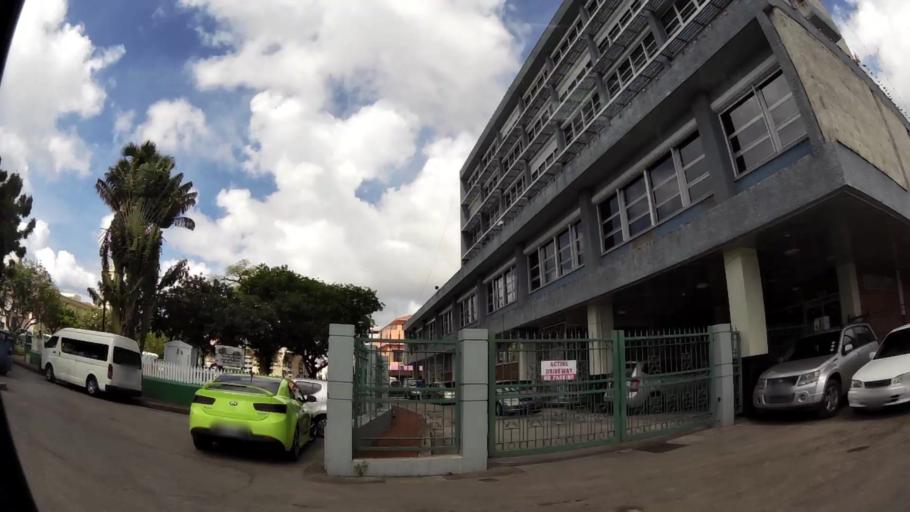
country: BB
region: Saint Michael
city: Bridgetown
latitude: 13.0965
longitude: -59.6135
